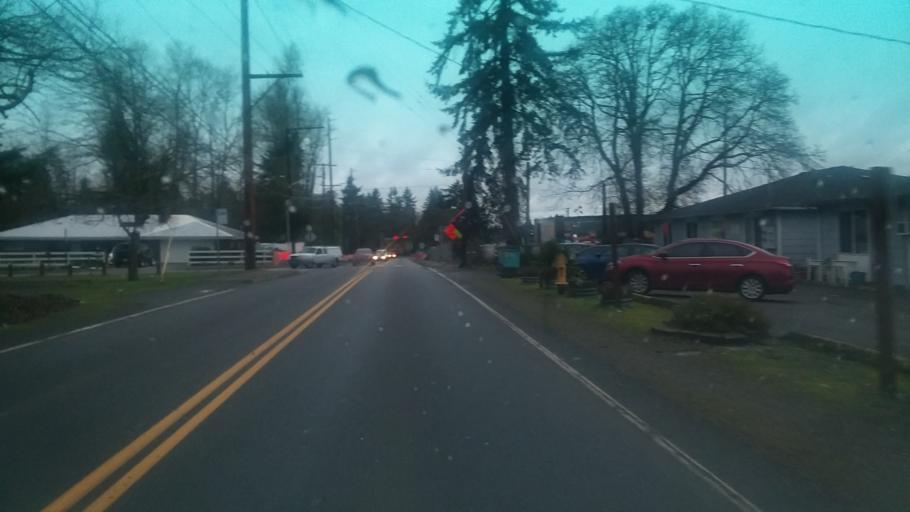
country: US
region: Washington
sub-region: Pierce County
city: Fort Lewis
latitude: 47.1263
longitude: -122.5460
